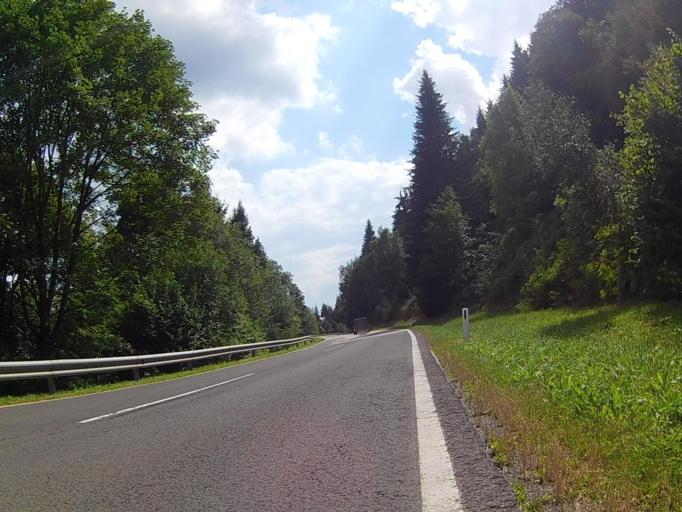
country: AT
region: Styria
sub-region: Politischer Bezirk Deutschlandsberg
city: Soboth
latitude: 46.6932
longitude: 15.1022
